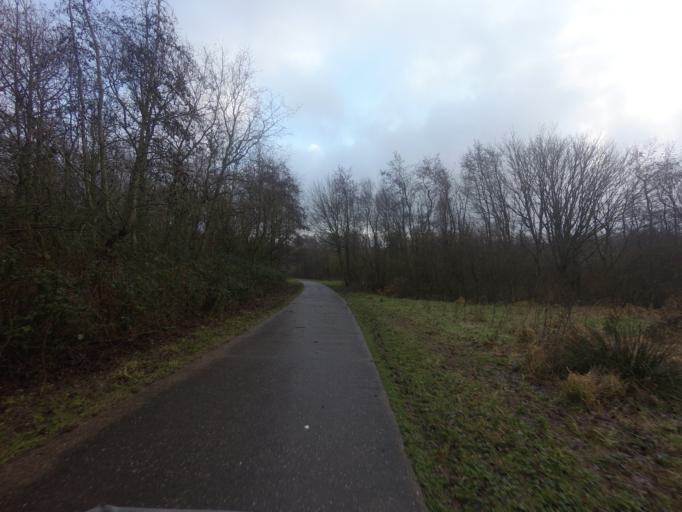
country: NL
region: North Holland
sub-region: Gemeente Texel
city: Den Burg
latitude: 53.1655
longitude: 4.8475
